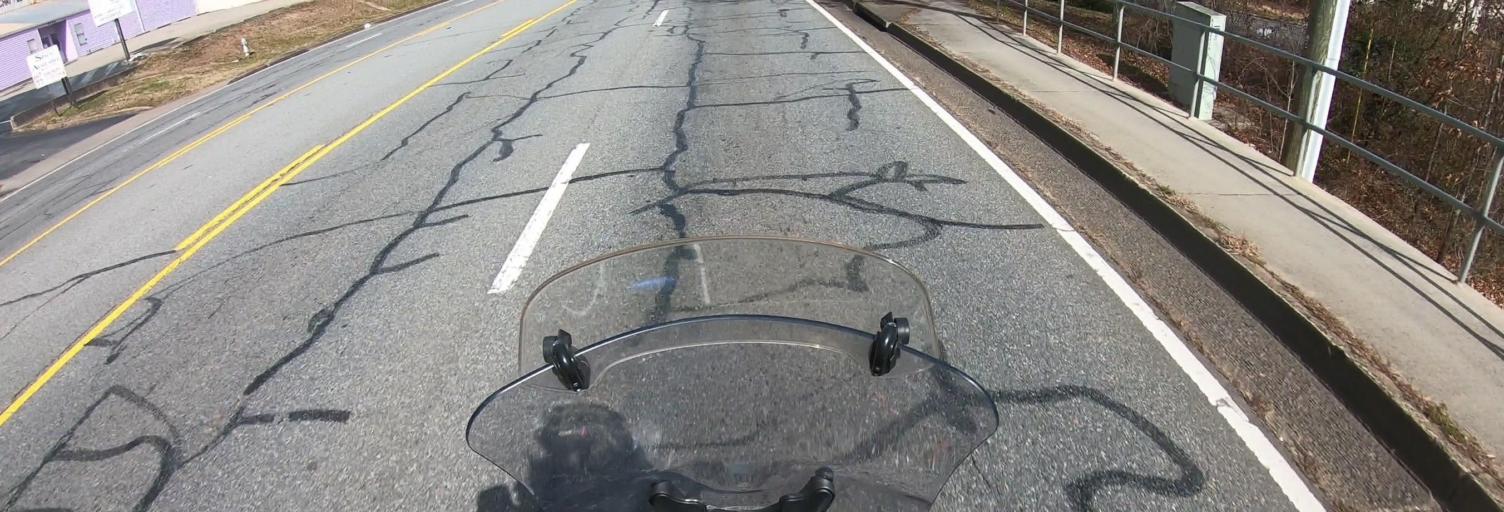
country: US
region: Georgia
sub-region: Cherokee County
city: Woodstock
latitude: 34.0471
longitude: -84.5284
